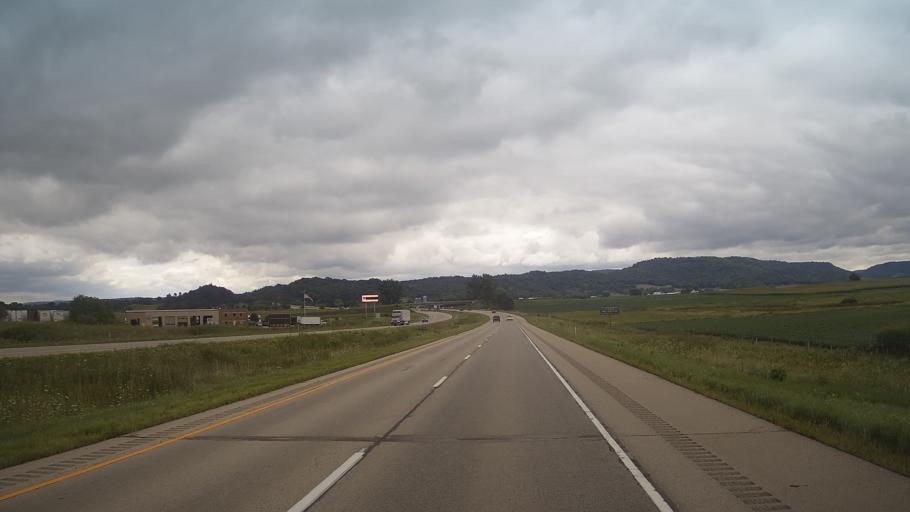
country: US
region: Wisconsin
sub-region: La Crosse County
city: Bangor
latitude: 43.8892
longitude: -91.0180
